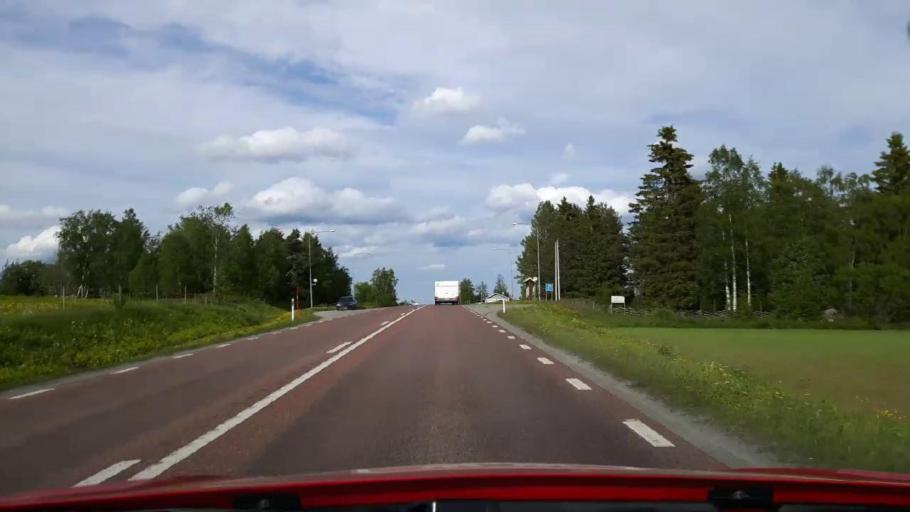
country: SE
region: Jaemtland
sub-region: OEstersunds Kommun
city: Brunflo
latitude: 63.0451
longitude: 14.8199
